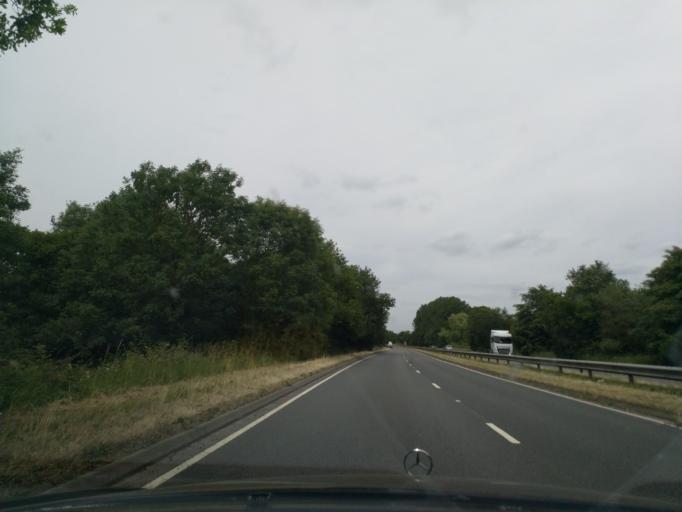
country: GB
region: England
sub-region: Solihull
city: Hampton in Arden
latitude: 52.4262
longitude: -1.6775
